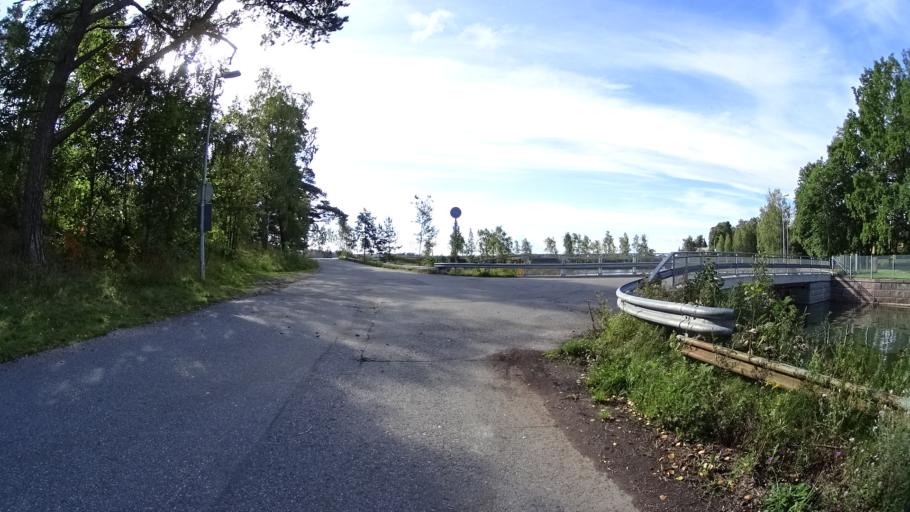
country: FI
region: Uusimaa
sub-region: Helsinki
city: Teekkarikylae
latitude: 60.1890
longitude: 24.8734
